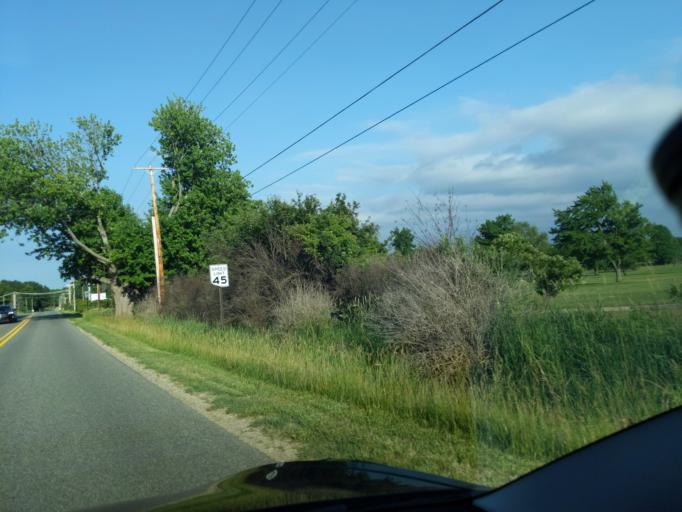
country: US
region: Michigan
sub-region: Muskegon County
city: Whitehall
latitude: 43.4030
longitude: -86.3200
